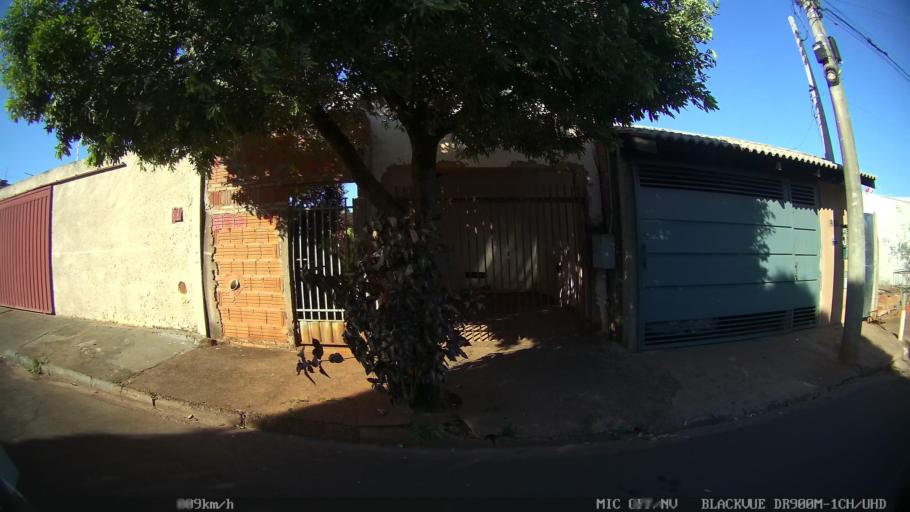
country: BR
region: Sao Paulo
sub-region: Olimpia
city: Olimpia
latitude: -20.7262
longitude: -48.9076
